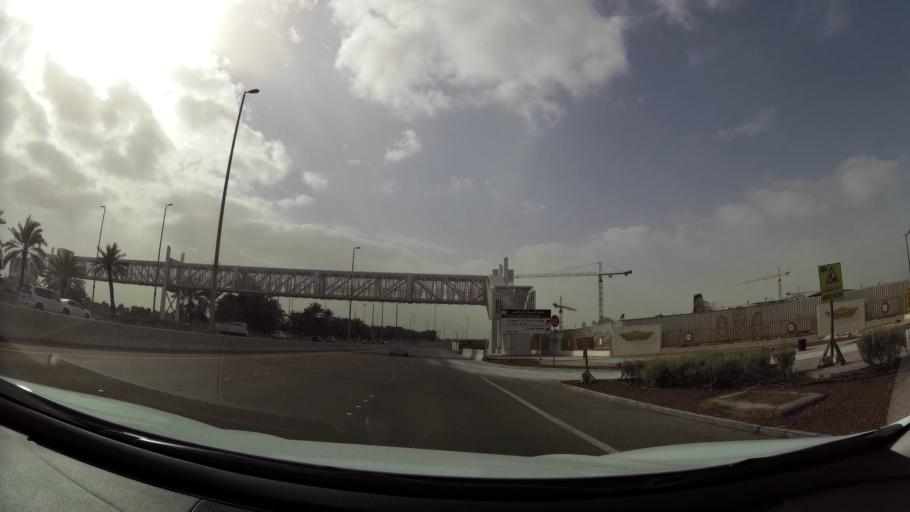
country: AE
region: Abu Dhabi
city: Abu Dhabi
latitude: 24.4114
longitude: 54.4779
